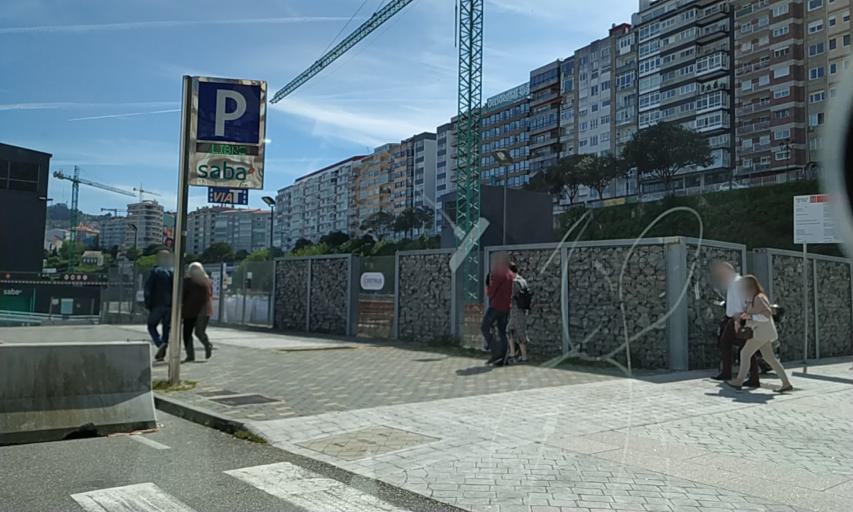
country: ES
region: Galicia
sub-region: Provincia de Pontevedra
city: Vigo
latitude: 42.2342
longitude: -8.7145
